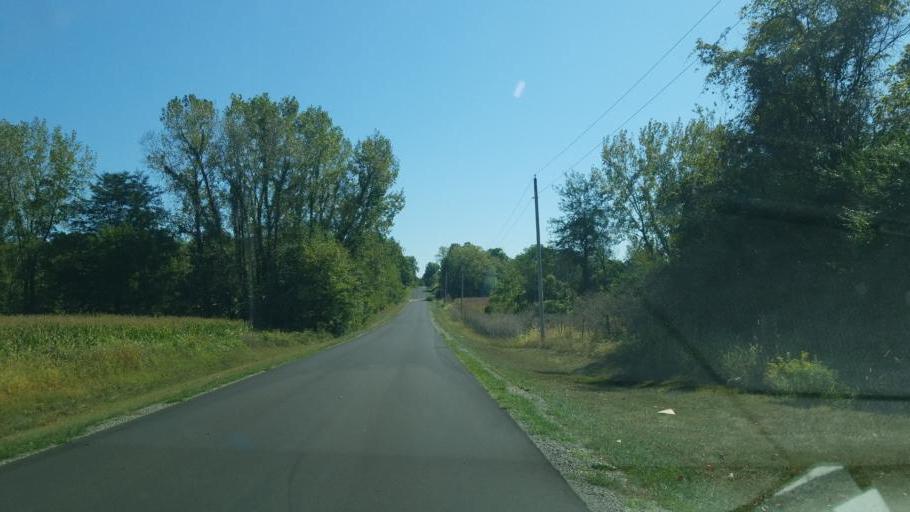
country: US
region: Ohio
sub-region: Logan County
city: Bellefontaine
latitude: 40.4110
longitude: -83.7720
